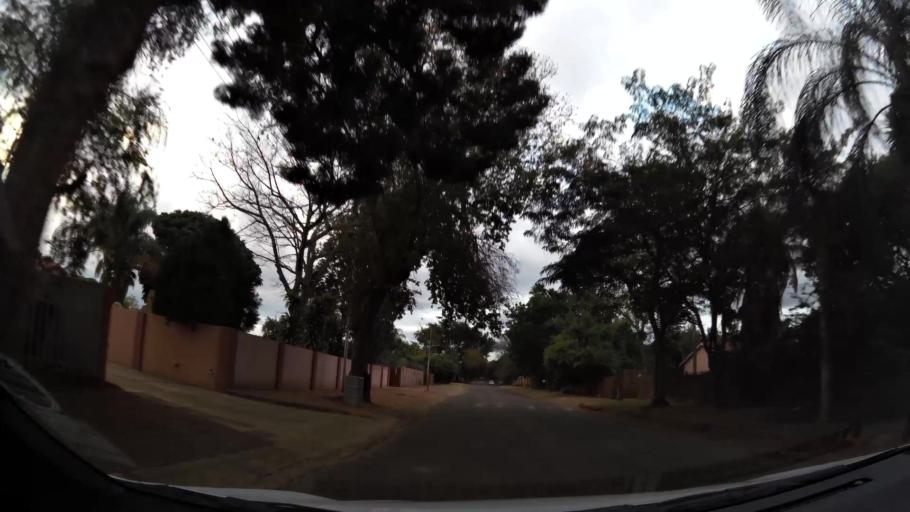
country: ZA
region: Limpopo
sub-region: Waterberg District Municipality
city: Mokopane
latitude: -24.1928
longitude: 28.9909
